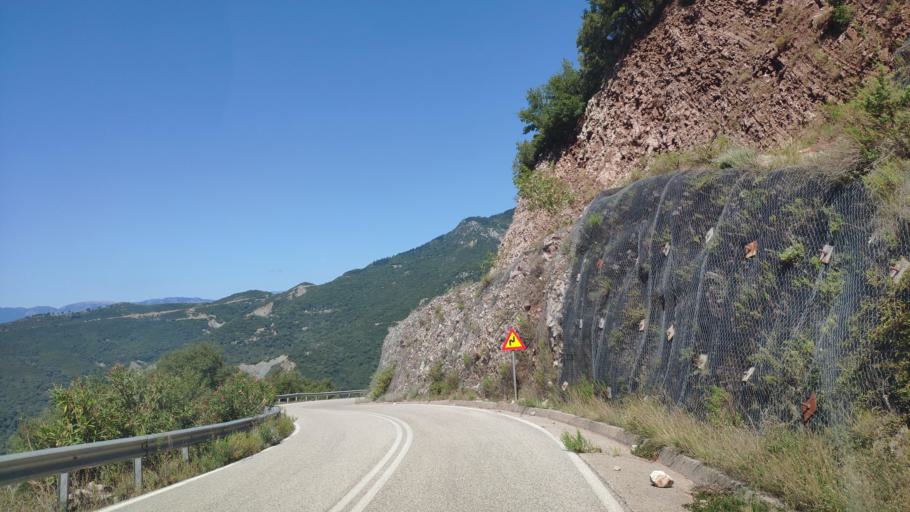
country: GR
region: Central Greece
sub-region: Nomos Evrytanias
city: Kerasochori
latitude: 39.0126
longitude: 21.5988
